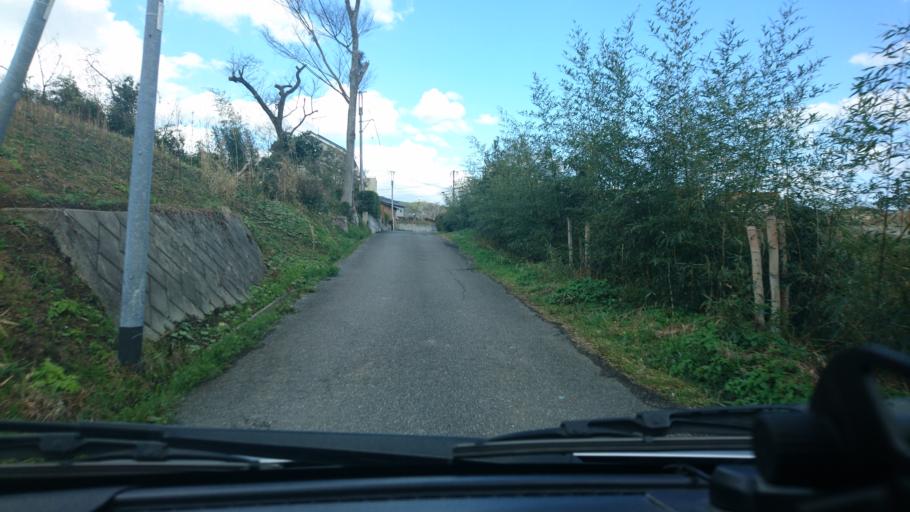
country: JP
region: Chiba
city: Kimitsu
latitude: 35.2874
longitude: 139.9844
